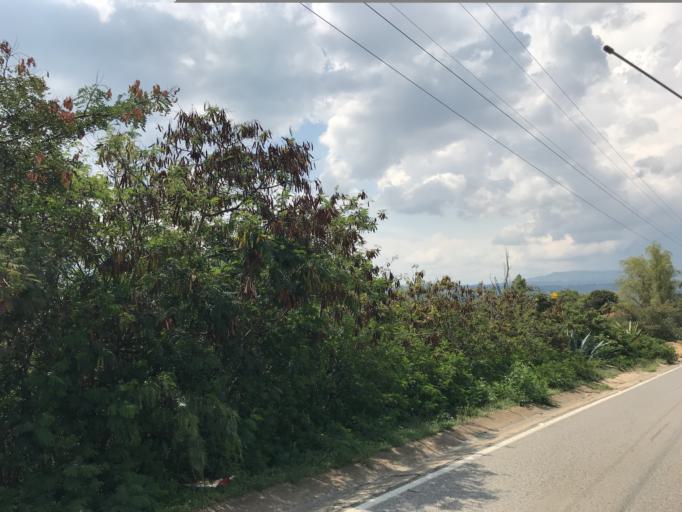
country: CO
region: Boyaca
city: Sachica
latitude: 5.6116
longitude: -73.5357
